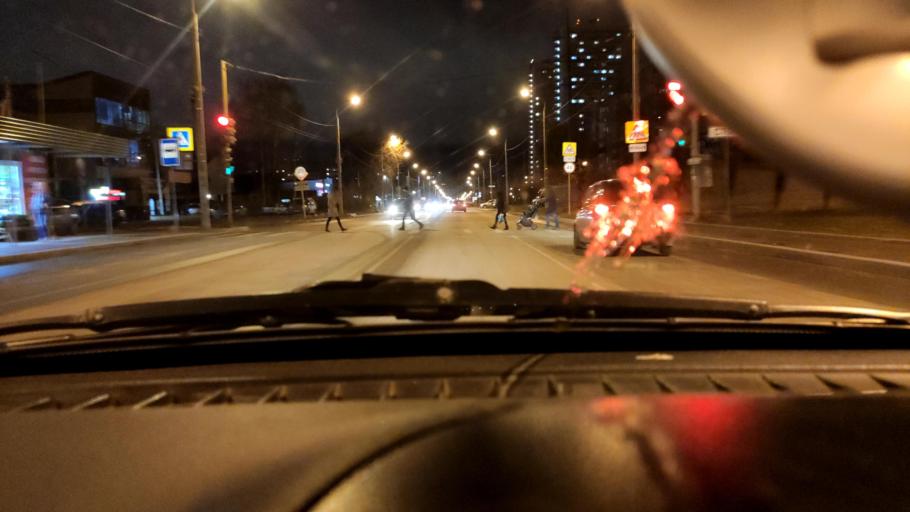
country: RU
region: Perm
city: Perm
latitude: 57.9754
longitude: 56.1978
